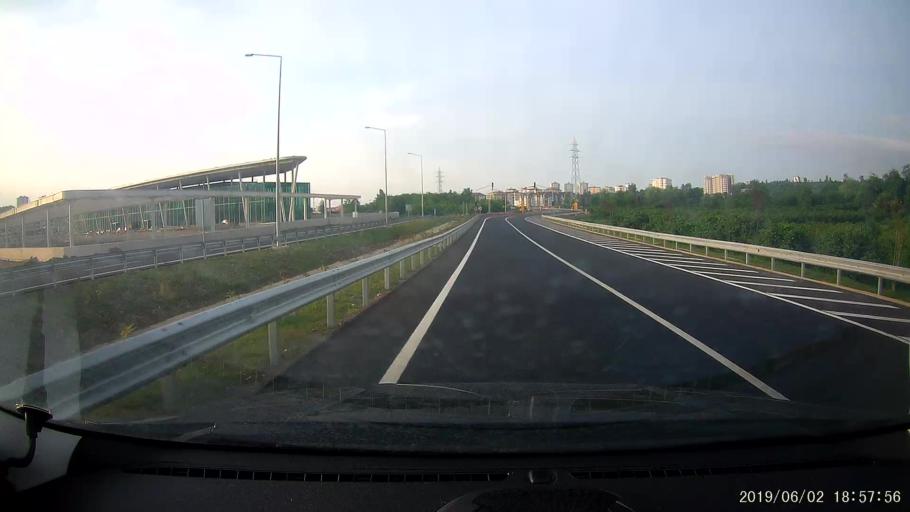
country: TR
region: Ordu
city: Ordu
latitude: 40.9565
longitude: 37.9034
